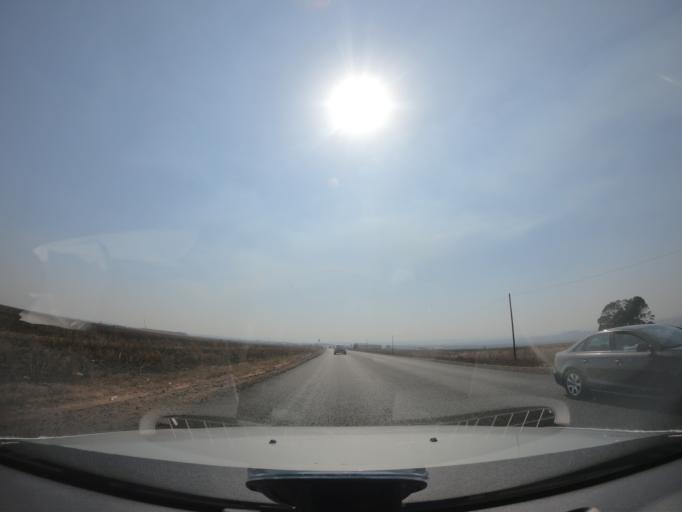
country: ZA
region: Mpumalanga
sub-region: Nkangala District Municipality
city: Middelburg
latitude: -25.8255
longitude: 29.4608
